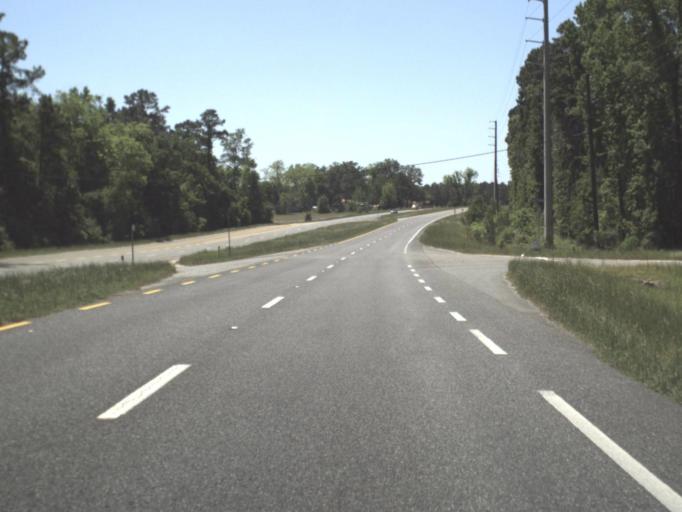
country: US
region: Florida
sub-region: Jefferson County
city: Monticello
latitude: 30.4586
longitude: -83.8928
